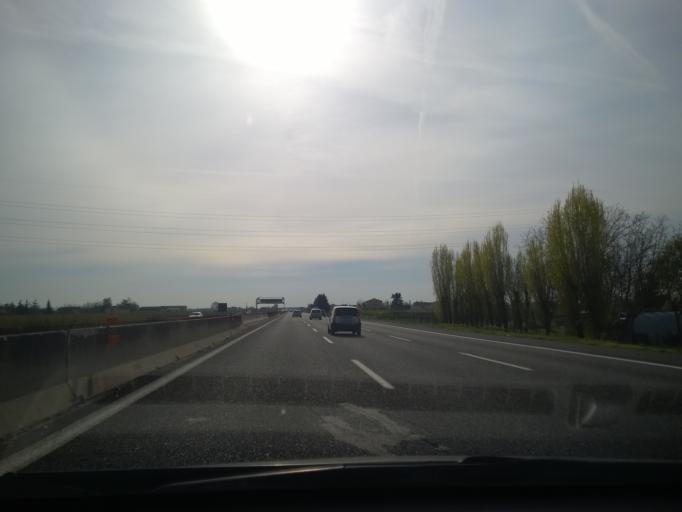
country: IT
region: Emilia-Romagna
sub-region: Forli-Cesena
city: Forli
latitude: 44.2490
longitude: 12.1014
